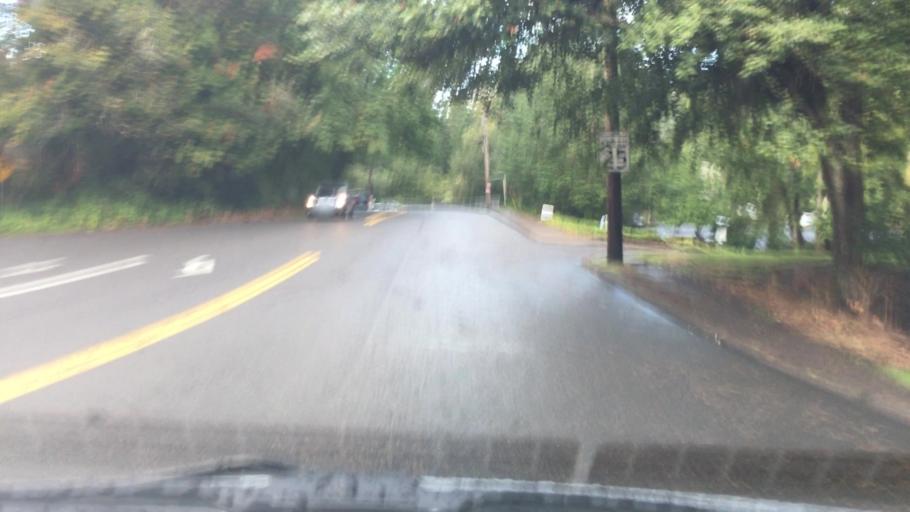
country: US
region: Oregon
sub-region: Multnomah County
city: Portland
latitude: 45.4821
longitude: -122.7077
